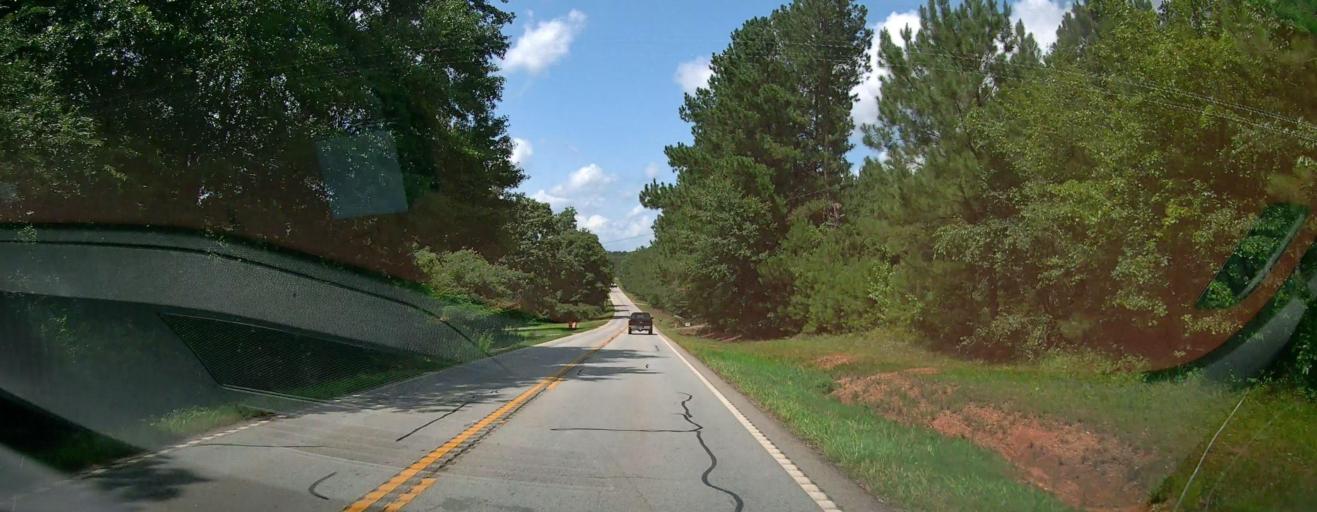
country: US
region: Georgia
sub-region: Heard County
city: Franklin
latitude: 33.3251
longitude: -85.1582
